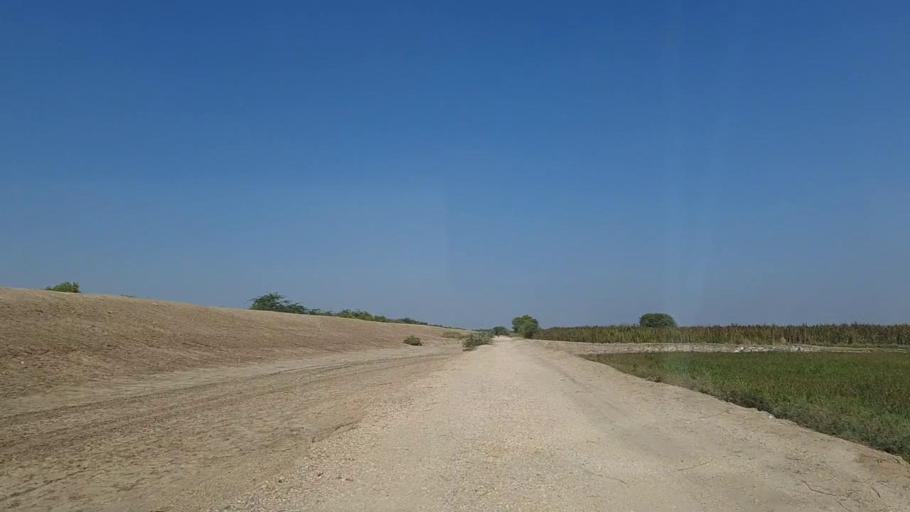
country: PK
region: Sindh
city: Chuhar Jamali
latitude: 24.4807
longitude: 68.0127
